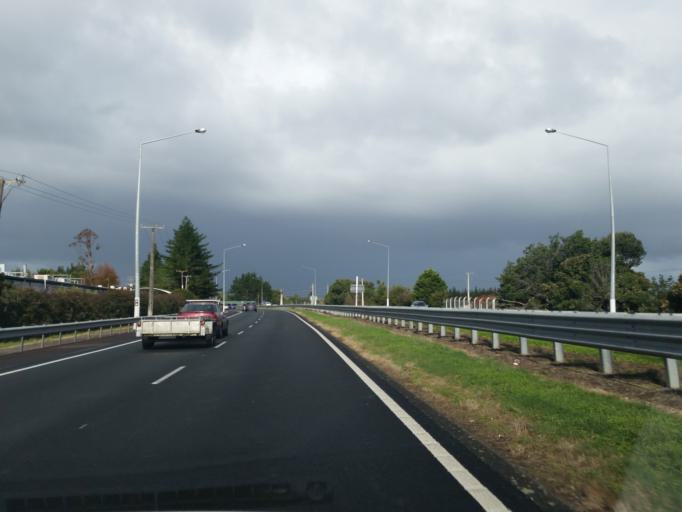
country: NZ
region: Auckland
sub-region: Auckland
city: Papakura
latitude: -37.1136
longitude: 174.9482
